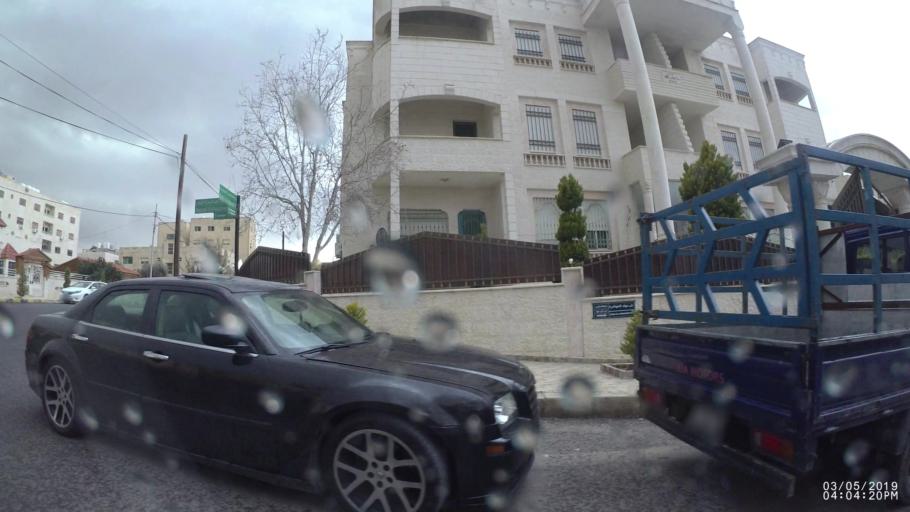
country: JO
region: Amman
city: Amman
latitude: 32.0071
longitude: 35.9574
